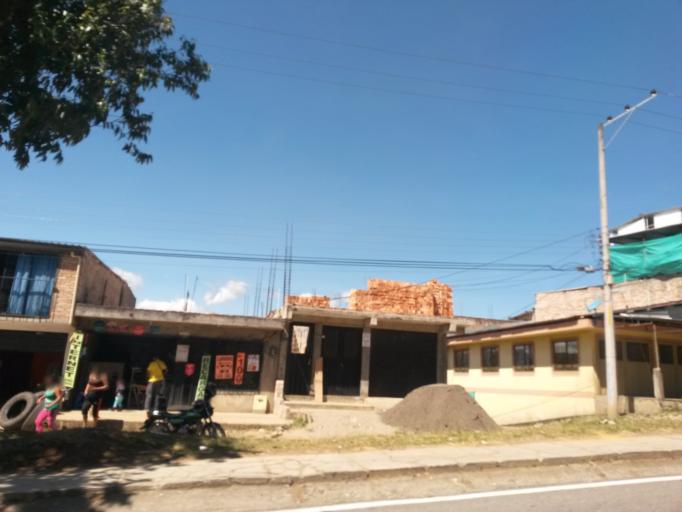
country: CO
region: Cauca
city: Popayan
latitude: 2.4573
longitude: -76.6455
